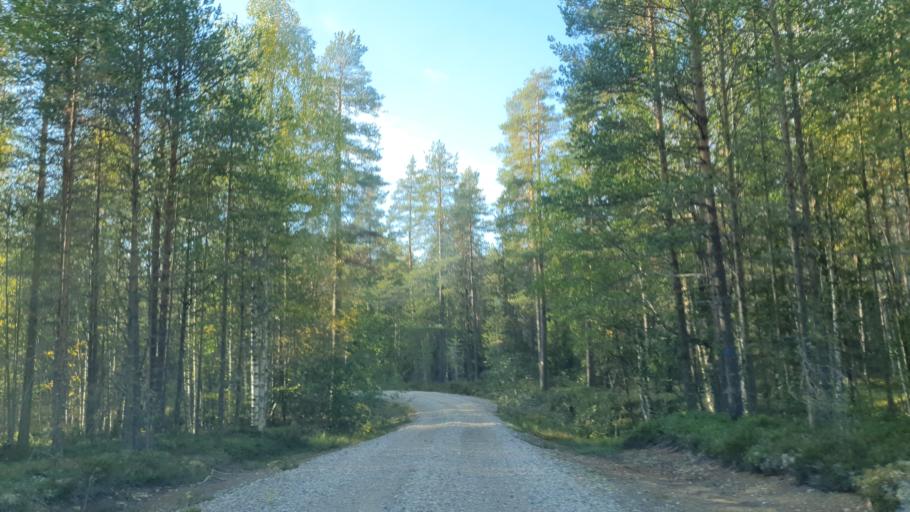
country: FI
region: Kainuu
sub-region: Kehys-Kainuu
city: Kuhmo
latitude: 64.3282
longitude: 30.0341
